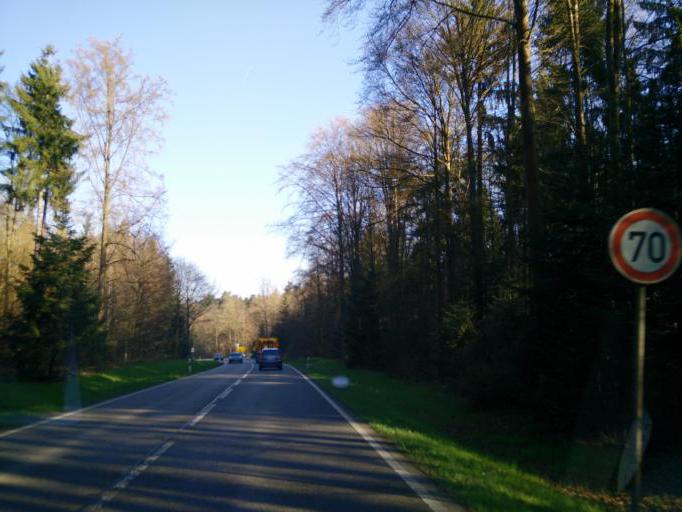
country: DE
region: Baden-Wuerttemberg
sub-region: Karlsruhe Region
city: Althengstett
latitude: 48.6794
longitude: 8.7759
